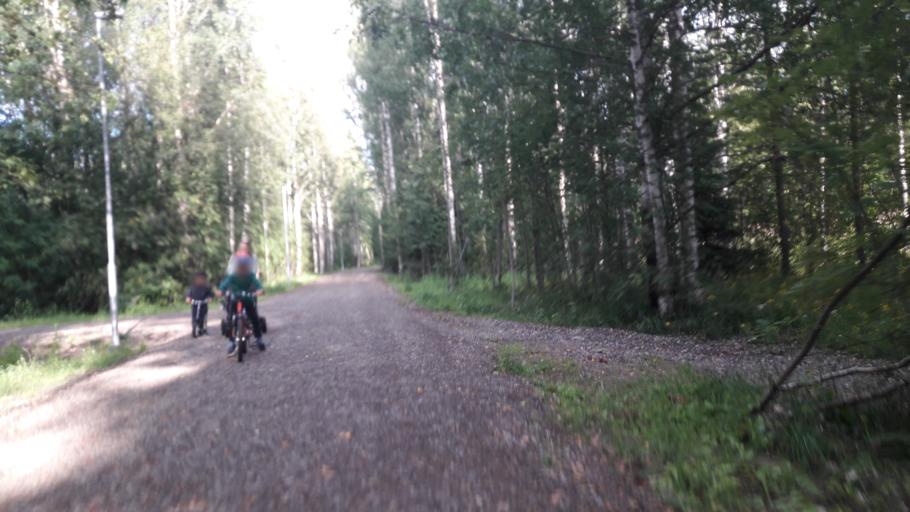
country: FI
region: North Karelia
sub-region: Joensuu
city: Joensuu
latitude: 62.5760
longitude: 29.7940
